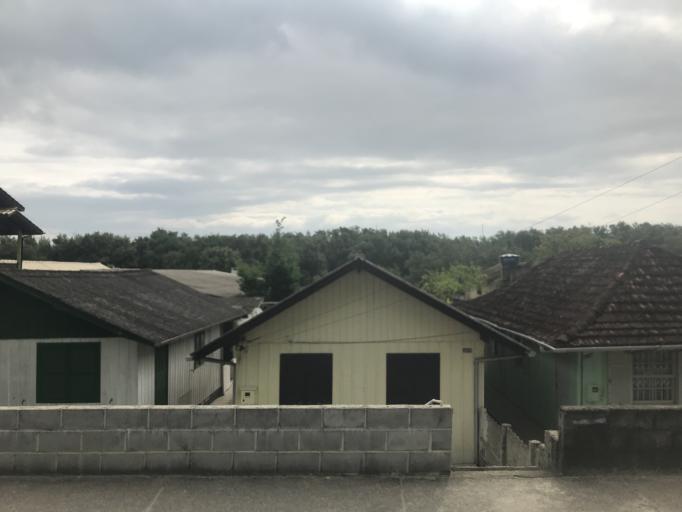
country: BR
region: Santa Catarina
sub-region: Florianopolis
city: Costeira do Pirajubae
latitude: -27.6436
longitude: -48.5220
